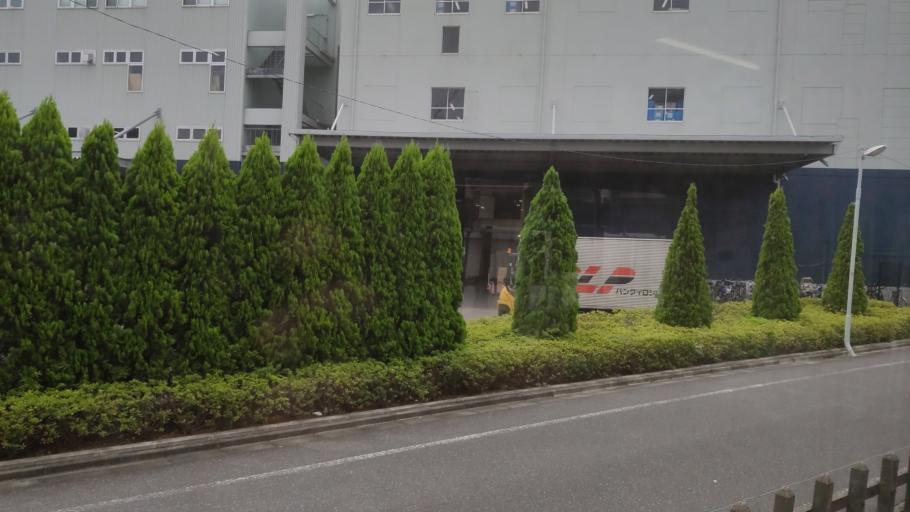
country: JP
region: Chiba
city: Matsudo
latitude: 35.7356
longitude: 139.8398
